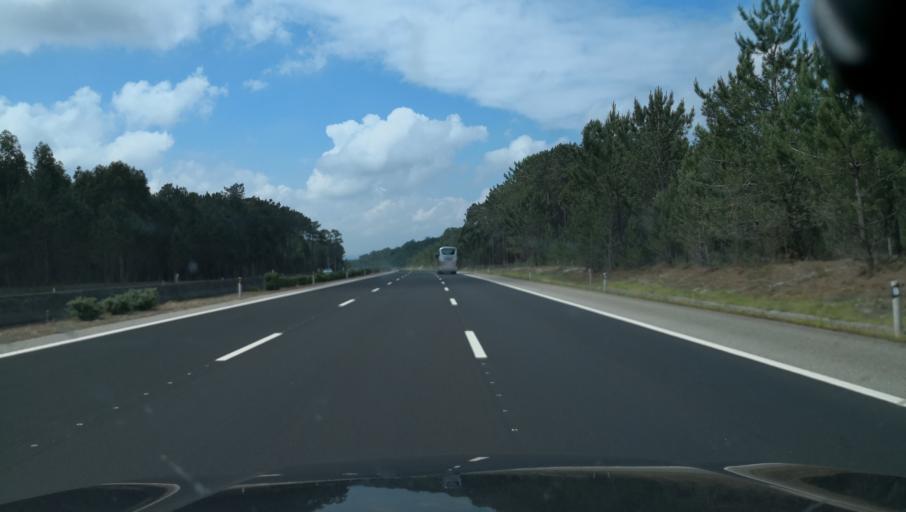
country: PT
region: Leiria
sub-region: Alcobaca
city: Pataias
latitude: 39.6666
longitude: -8.9541
